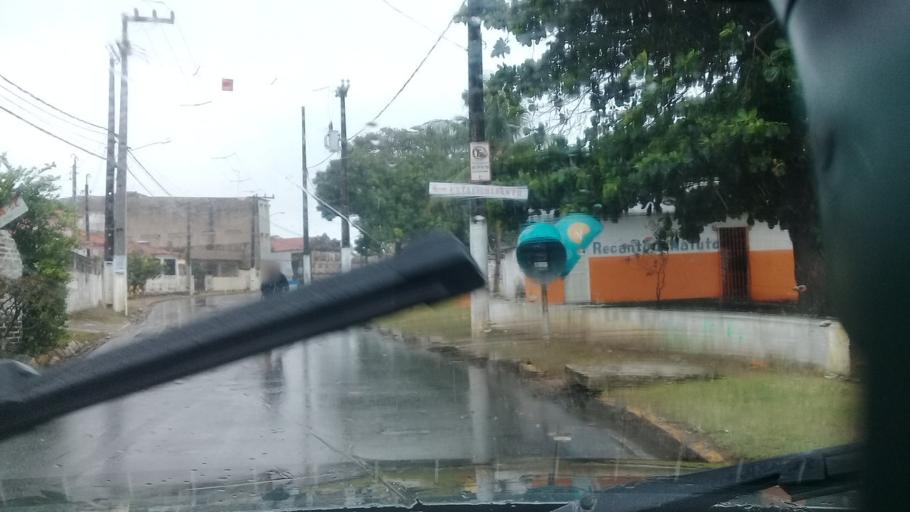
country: BR
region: Pernambuco
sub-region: Itamaraca
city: Itamaraca
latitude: -7.7314
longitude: -34.8261
